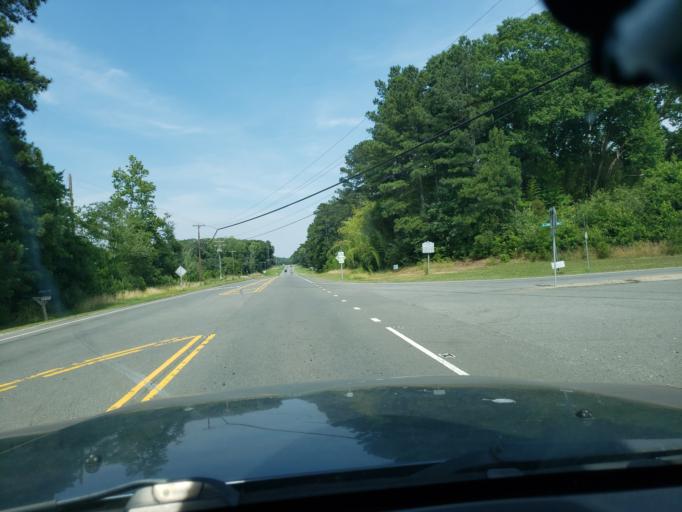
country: US
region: North Carolina
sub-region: Orange County
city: Carrboro
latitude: 35.9240
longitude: -79.1751
